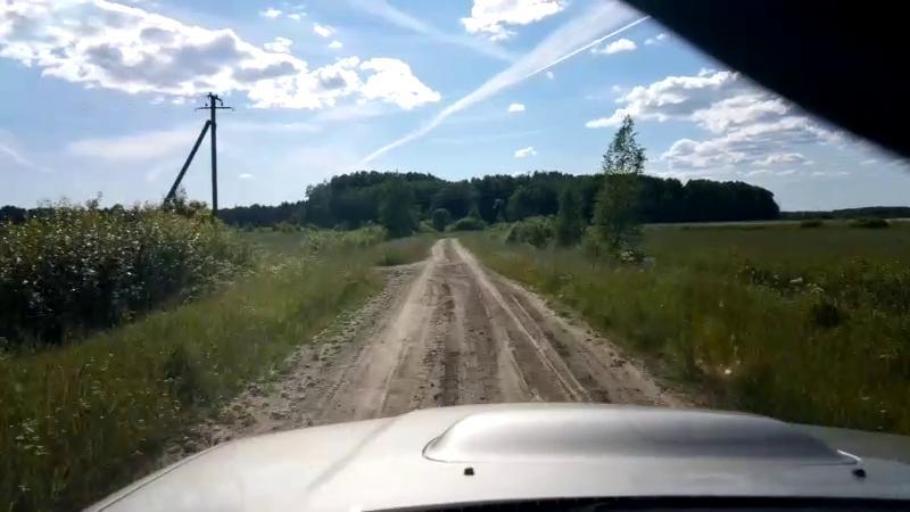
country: EE
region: Paernumaa
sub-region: Sauga vald
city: Sauga
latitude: 58.4918
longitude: 24.5533
